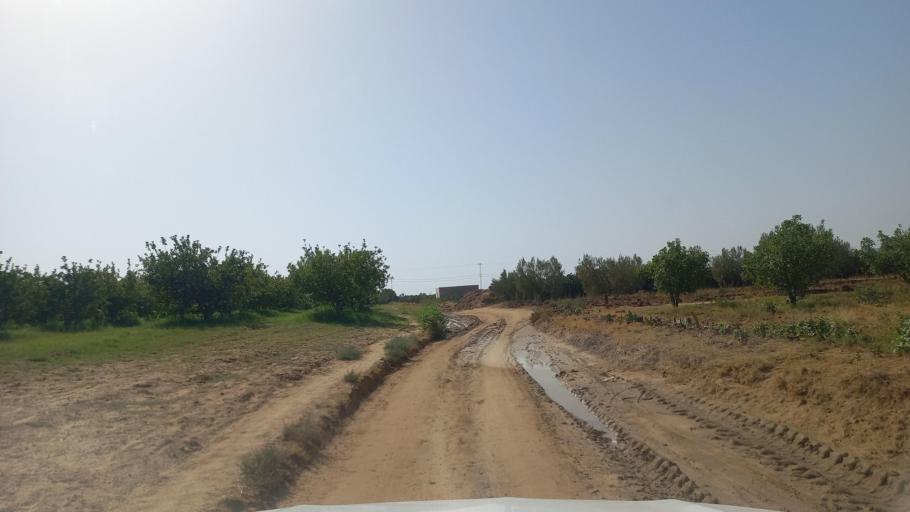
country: TN
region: Al Qasrayn
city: Kasserine
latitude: 35.2420
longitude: 9.0359
